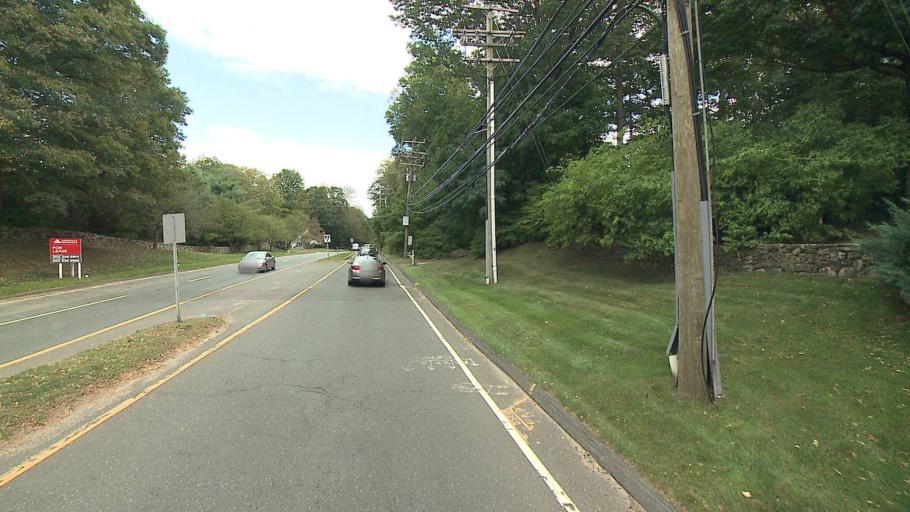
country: US
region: Connecticut
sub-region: Fairfield County
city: Wilton
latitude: 41.1804
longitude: -73.4135
